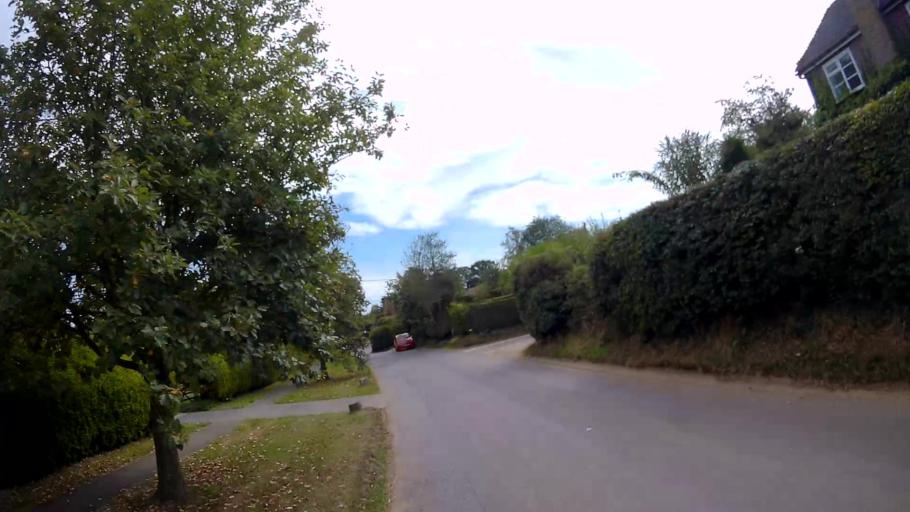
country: GB
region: England
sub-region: Hampshire
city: Long Sutton
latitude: 51.2211
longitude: -0.9446
